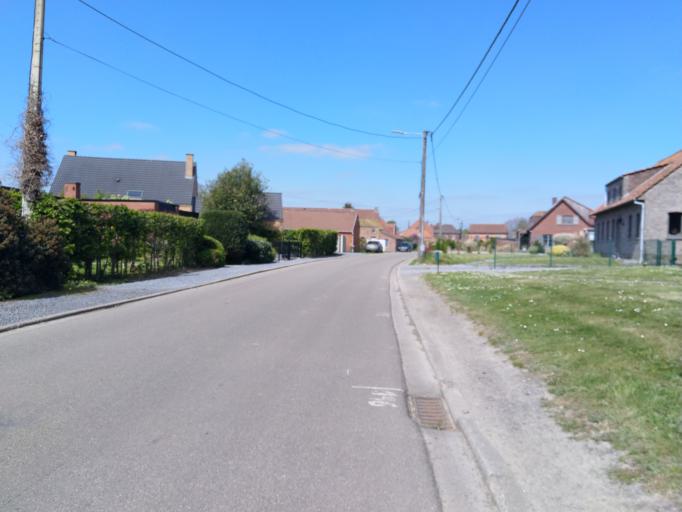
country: BE
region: Wallonia
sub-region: Province du Hainaut
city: Lens
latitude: 50.5266
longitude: 3.8535
